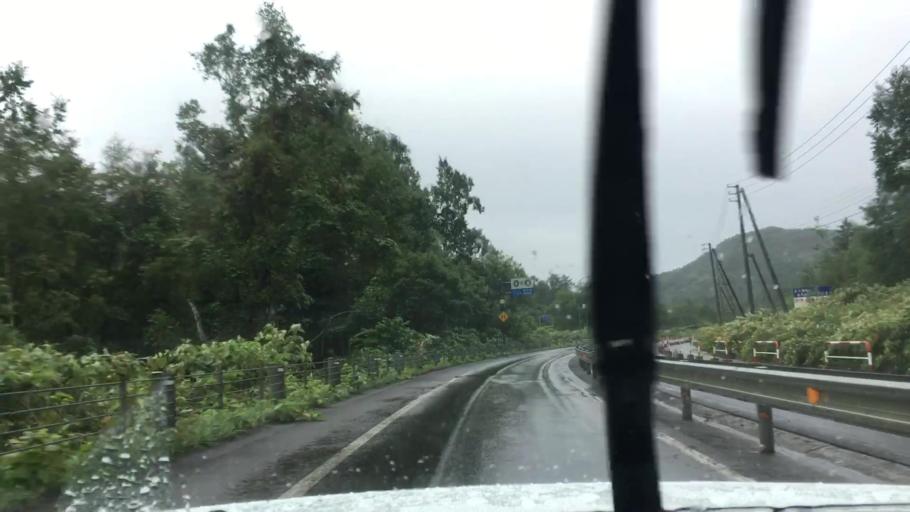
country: JP
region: Hokkaido
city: Niseko Town
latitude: 42.8315
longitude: 141.0094
